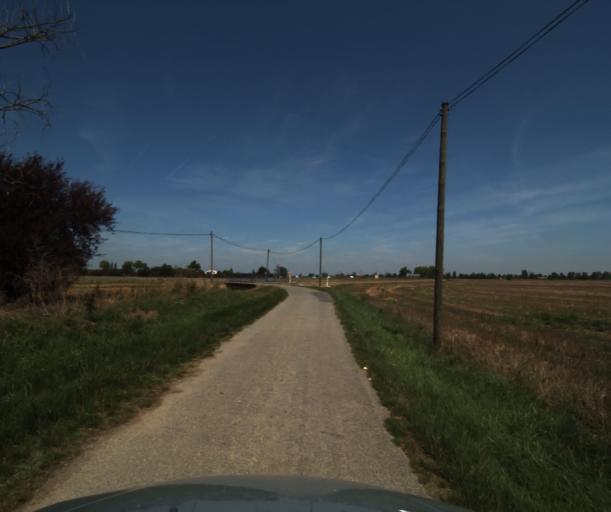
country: FR
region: Midi-Pyrenees
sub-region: Departement de la Haute-Garonne
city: Labastidette
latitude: 43.4625
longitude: 1.2684
